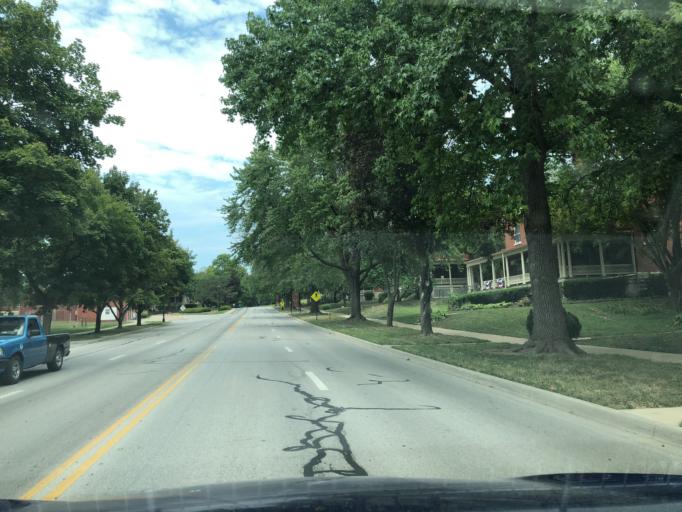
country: US
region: Kansas
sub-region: Leavenworth County
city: Leavenworth
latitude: 39.3507
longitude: -94.9185
